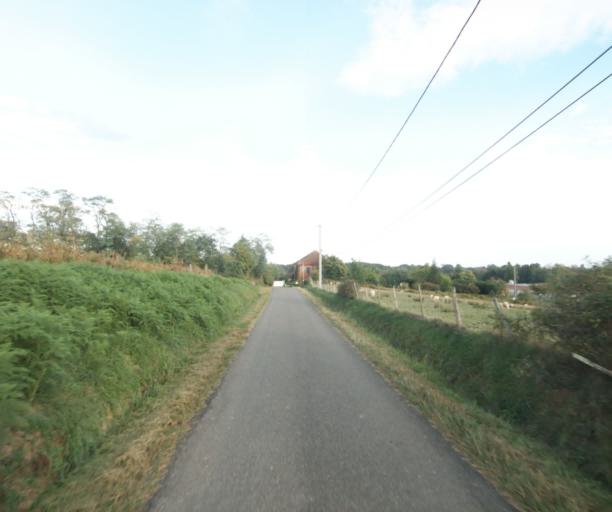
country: FR
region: Midi-Pyrenees
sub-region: Departement du Gers
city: Le Houga
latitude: 43.8411
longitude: -0.1064
